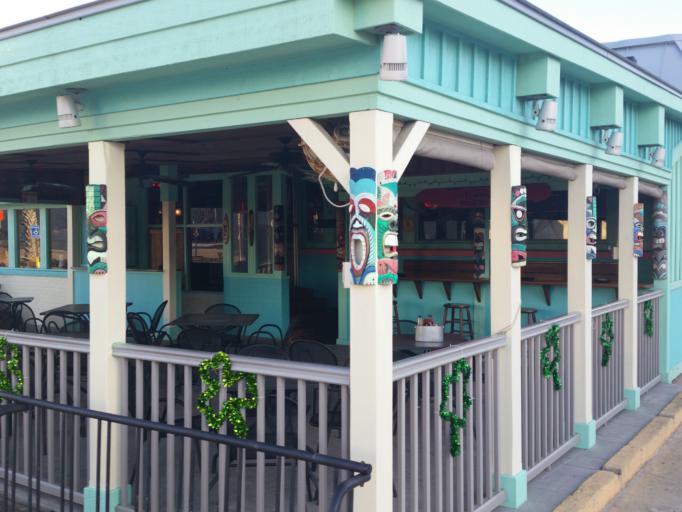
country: US
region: Virginia
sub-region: City of Virginia Beach
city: Virginia Beach
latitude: 36.8518
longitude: -75.9772
